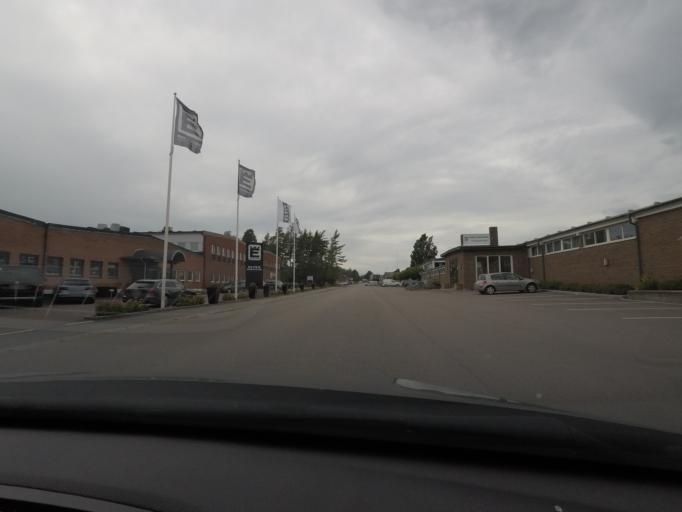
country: SE
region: Skane
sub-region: Osby Kommun
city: Osby
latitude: 56.3814
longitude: 13.9838
